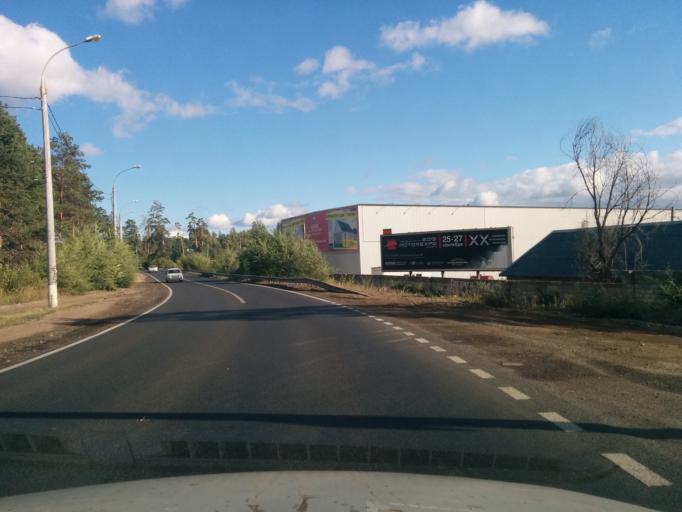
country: RU
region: Samara
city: Tol'yatti
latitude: 53.4774
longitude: 49.3236
